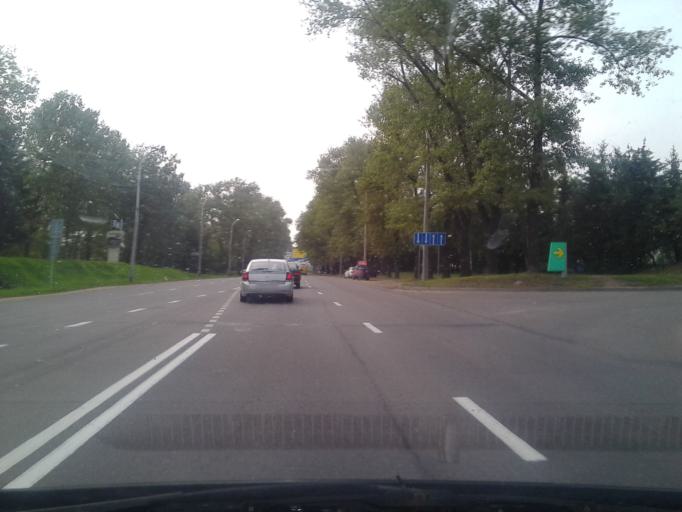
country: BY
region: Minsk
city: Zhdanovichy
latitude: 53.9309
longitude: 27.4729
